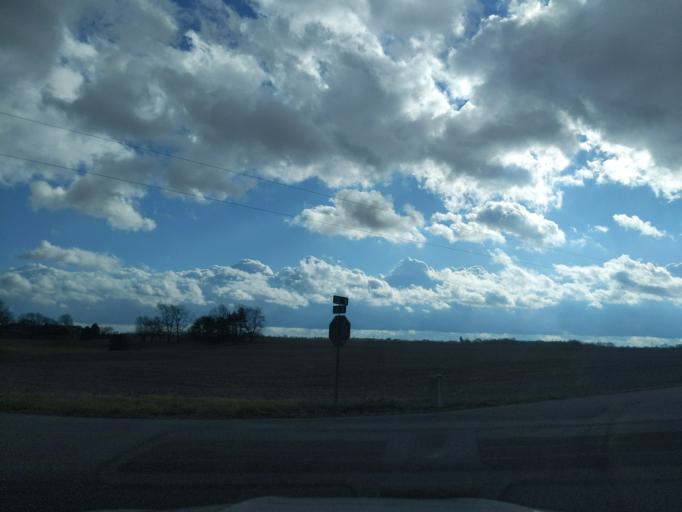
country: US
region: Indiana
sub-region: Decatur County
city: Greensburg
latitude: 39.4095
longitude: -85.5078
